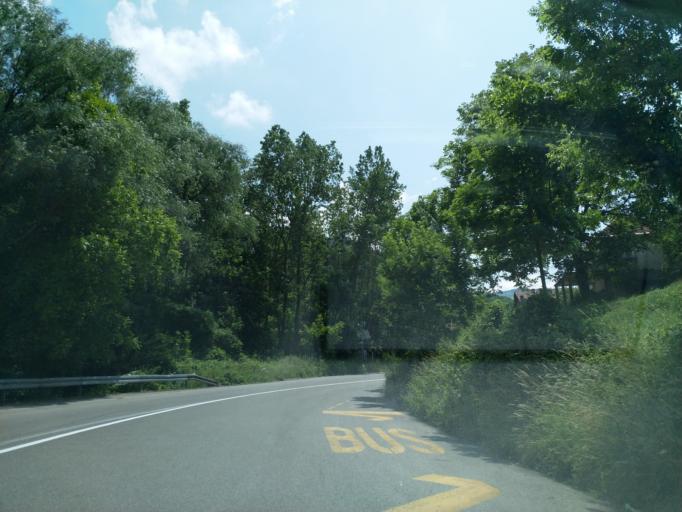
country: RS
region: Central Serbia
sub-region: Rasinski Okrug
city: Aleksandrovac
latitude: 43.3147
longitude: 20.9183
